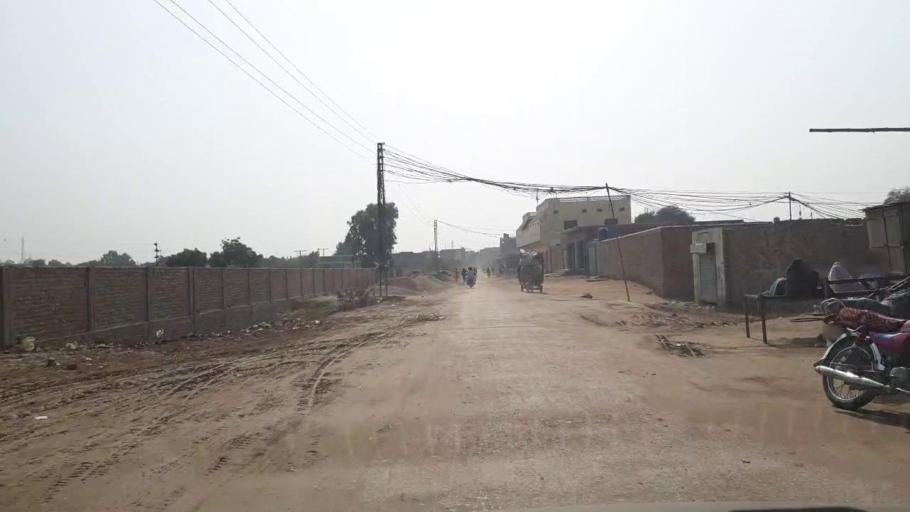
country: PK
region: Sindh
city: Bhit Shah
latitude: 25.8114
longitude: 68.4885
